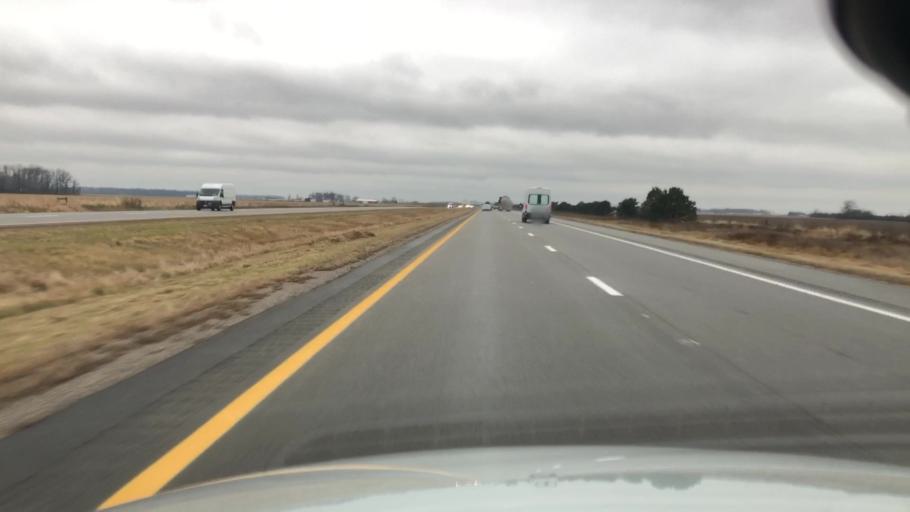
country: US
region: Ohio
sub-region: Van Wert County
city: Van Wert
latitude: 40.8699
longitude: -84.4867
